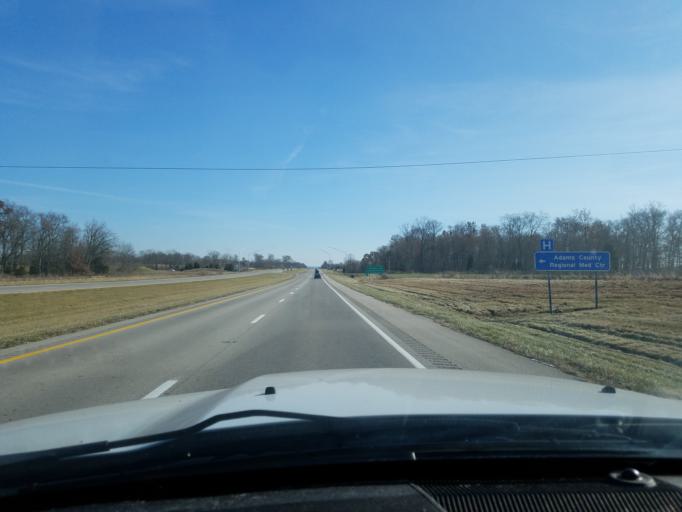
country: US
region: Ohio
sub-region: Adams County
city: Winchester
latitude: 38.9331
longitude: -83.5996
